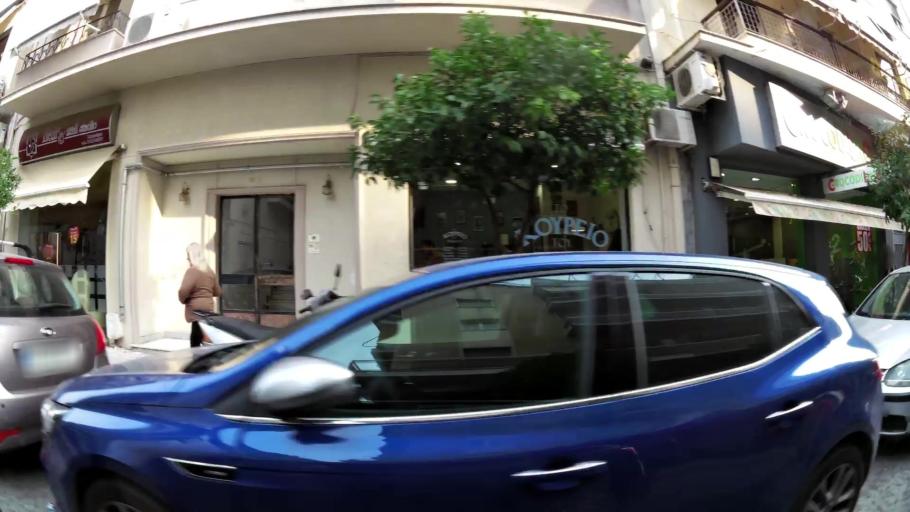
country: GR
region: Attica
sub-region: Nomarchia Athinas
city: Kipseli
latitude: 37.9913
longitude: 23.7480
